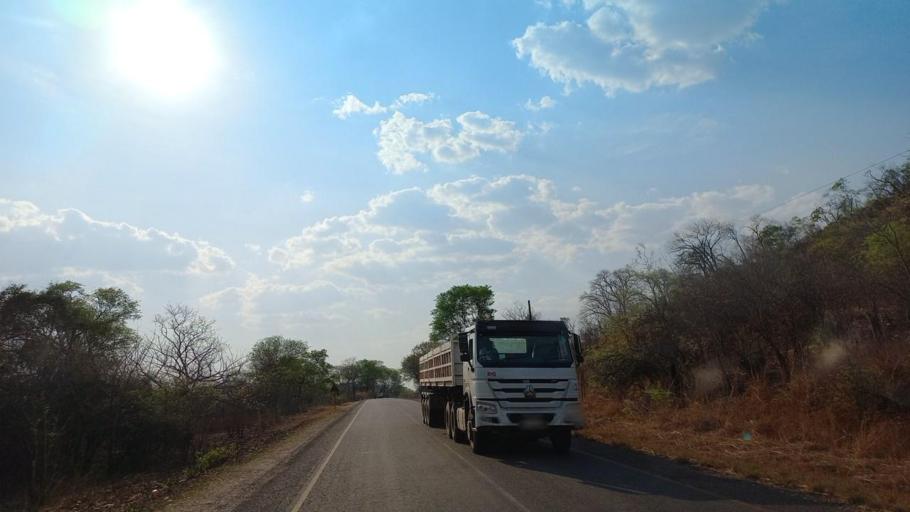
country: ZM
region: Lusaka
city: Luangwa
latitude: -14.9838
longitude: 30.1565
